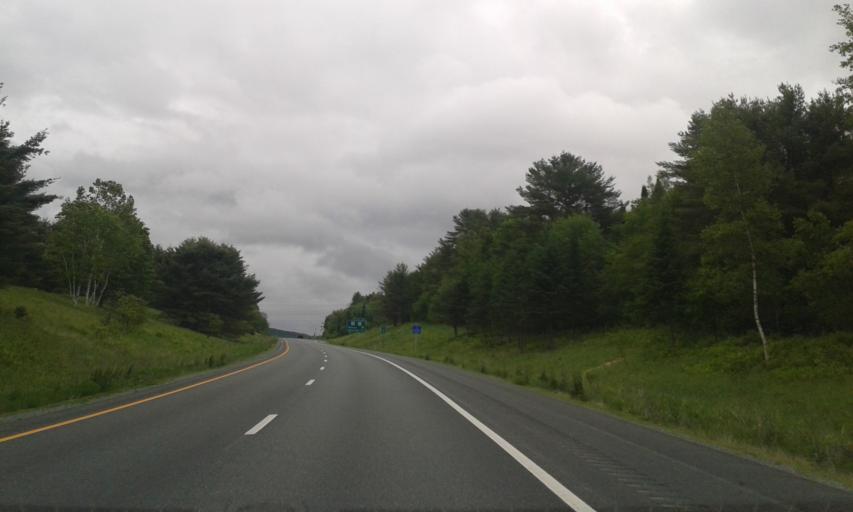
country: US
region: New Hampshire
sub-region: Grafton County
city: Littleton
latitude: 44.3343
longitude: -71.8860
